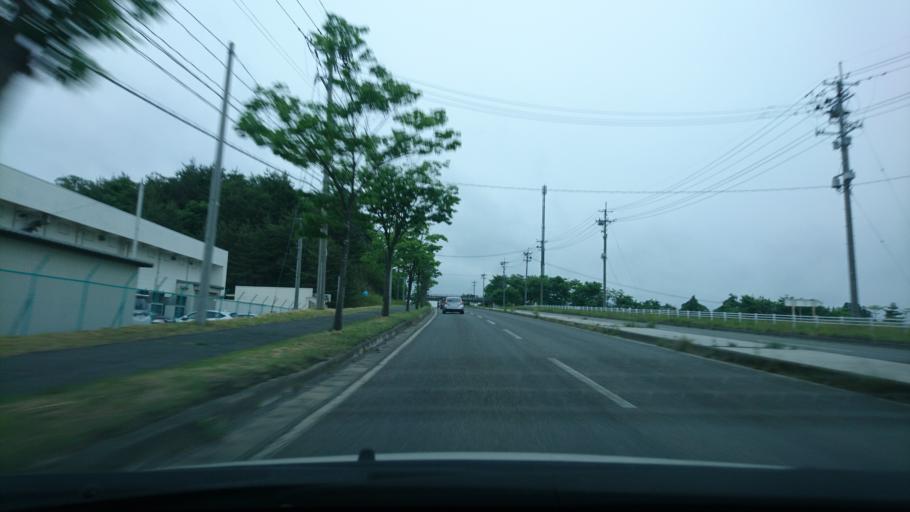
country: JP
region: Iwate
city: Ichinoseki
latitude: 38.9178
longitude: 141.1589
